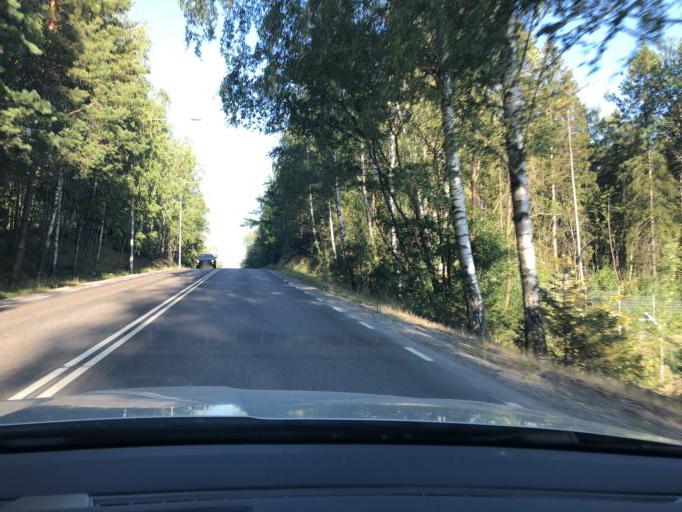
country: SE
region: Stockholm
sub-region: Sodertalje Kommun
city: Soedertaelje
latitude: 59.1828
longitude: 17.6016
